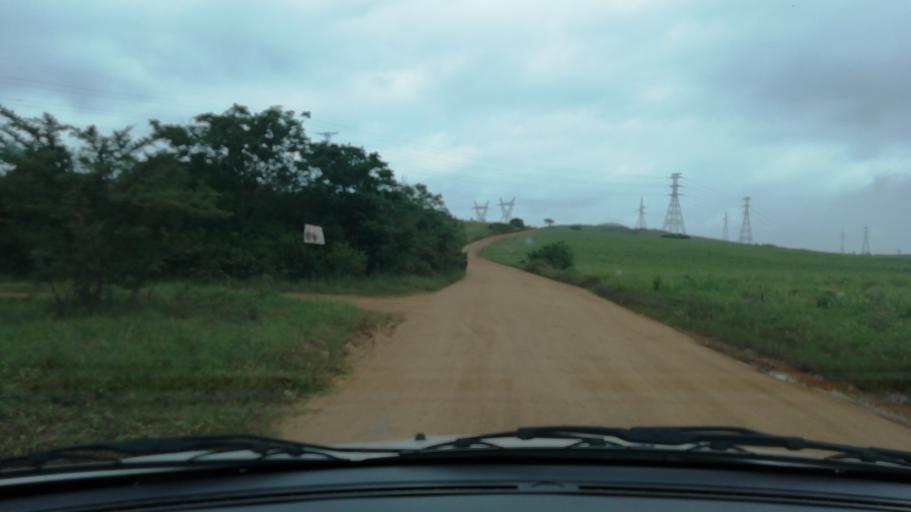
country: ZA
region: KwaZulu-Natal
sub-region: uThungulu District Municipality
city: Empangeni
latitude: -28.7337
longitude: 31.8990
